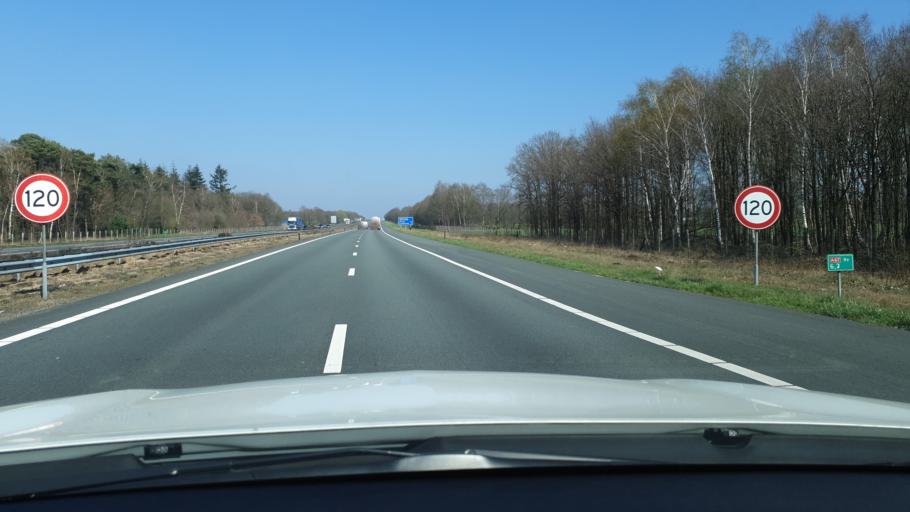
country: NL
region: North Brabant
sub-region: Gemeente Eersel
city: Eersel
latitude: 51.3552
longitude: 5.2830
